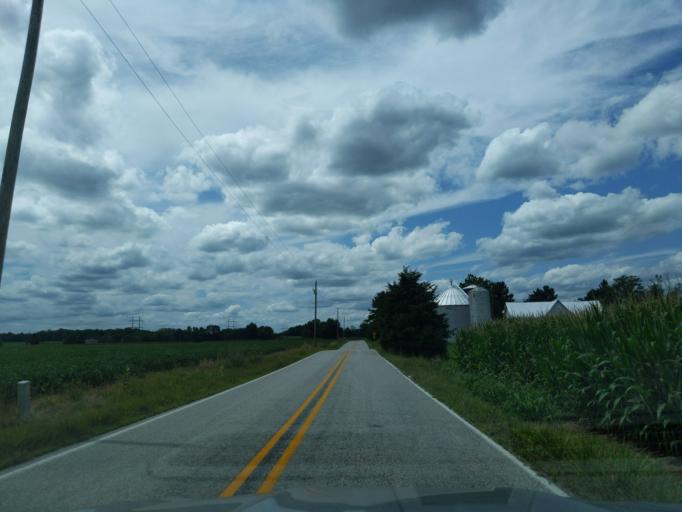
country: US
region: Indiana
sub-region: Ripley County
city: Osgood
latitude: 39.2160
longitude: -85.2704
